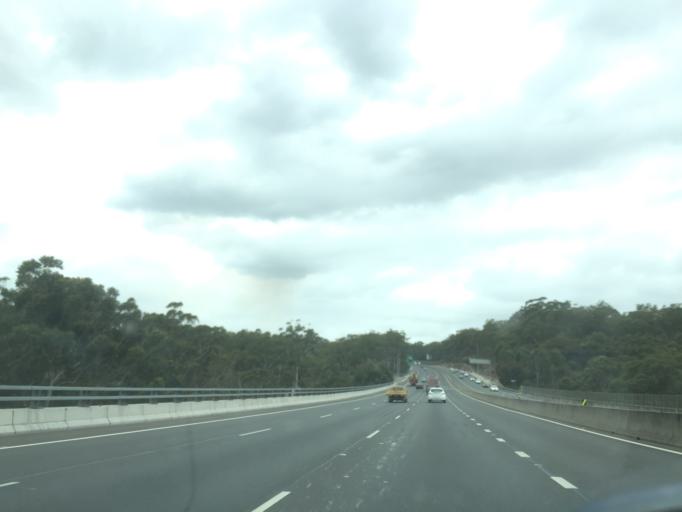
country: AU
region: New South Wales
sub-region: The Hills Shire
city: Baulkham Hills
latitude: -33.7669
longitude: 151.0042
